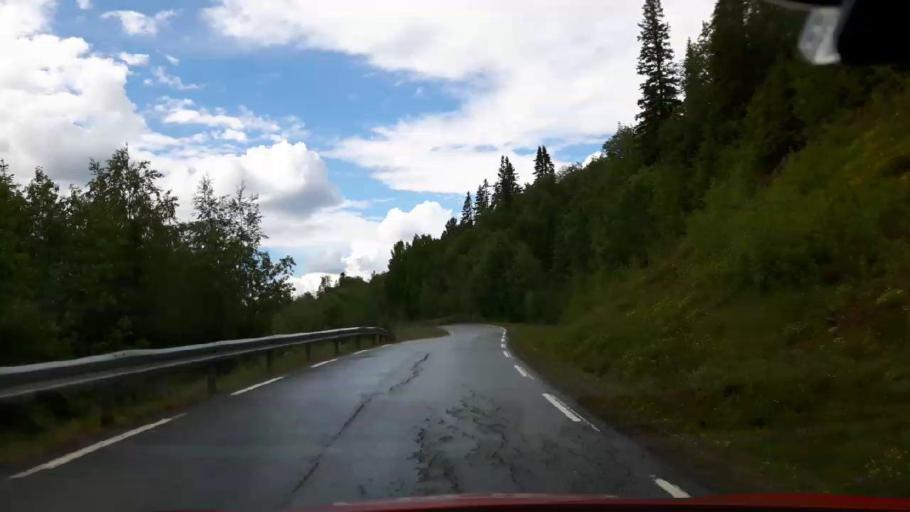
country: NO
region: Nord-Trondelag
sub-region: Lierne
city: Sandvika
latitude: 64.1052
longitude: 13.9924
